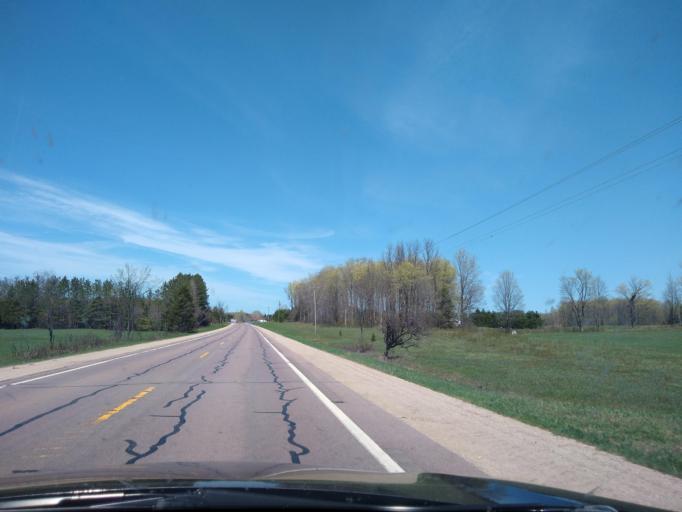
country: US
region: Michigan
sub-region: Marquette County
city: K. I. Sawyer Air Force Base
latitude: 46.2483
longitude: -87.0814
